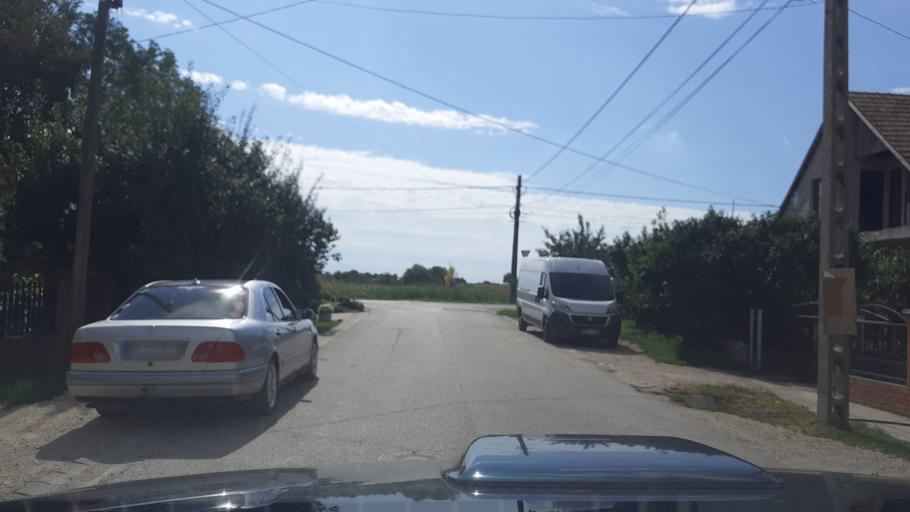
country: HU
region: Fejer
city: Seregelyes
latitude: 47.1072
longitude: 18.5787
